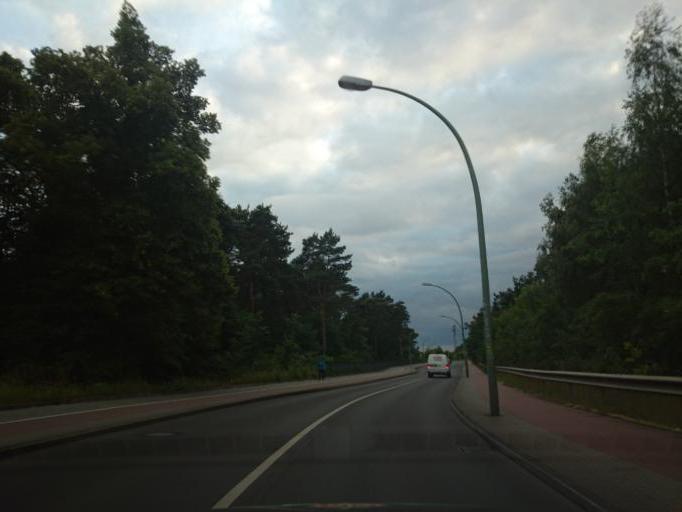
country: DE
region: Berlin
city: Karlshorst
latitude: 52.4695
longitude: 13.5570
